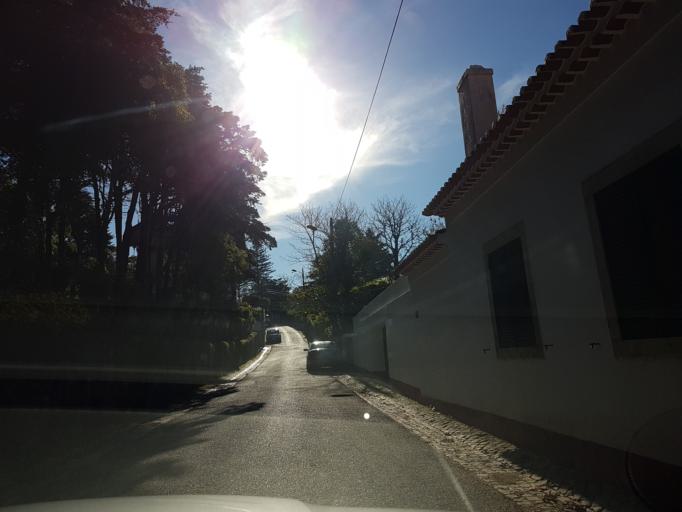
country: PT
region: Lisbon
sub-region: Sintra
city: Sintra
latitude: 38.7946
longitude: -9.3804
